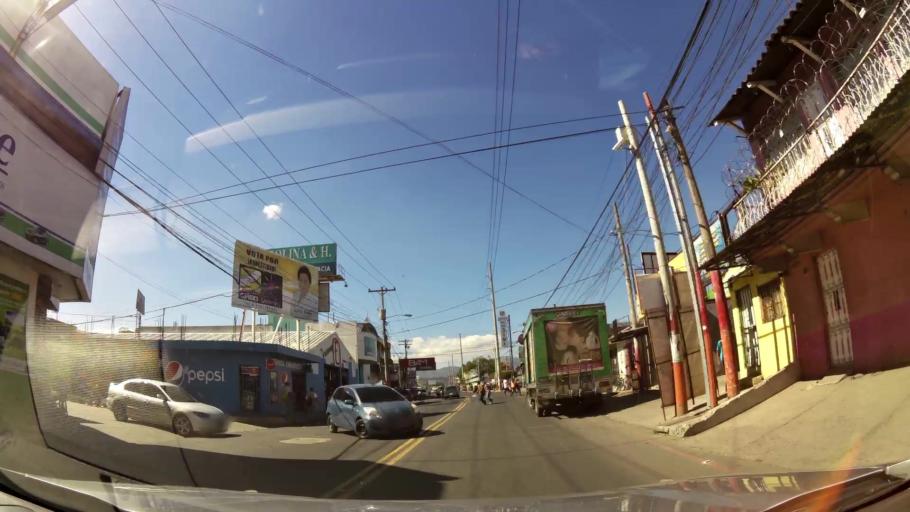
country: GT
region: Guatemala
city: Petapa
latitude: 14.5024
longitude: -90.5626
